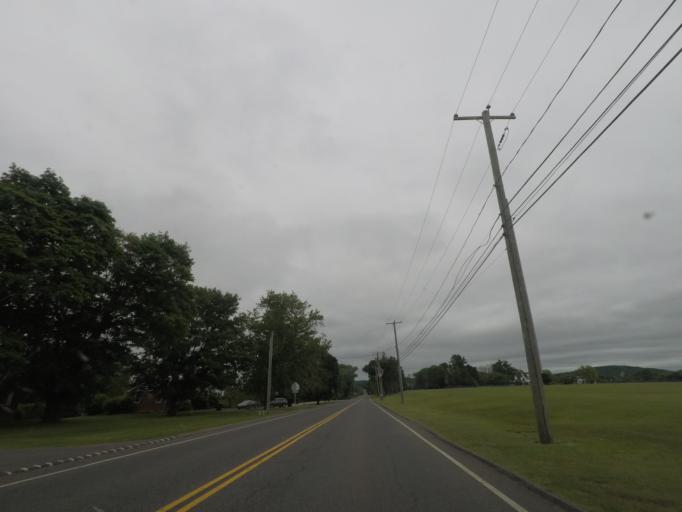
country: US
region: Connecticut
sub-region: Litchfield County
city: Canaan
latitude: 41.9412
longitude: -73.4386
